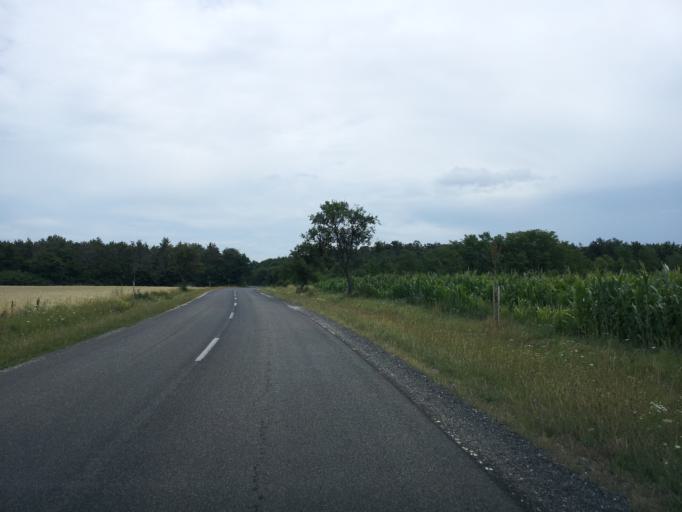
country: HU
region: Vas
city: Vasvar
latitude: 47.0478
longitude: 16.8277
